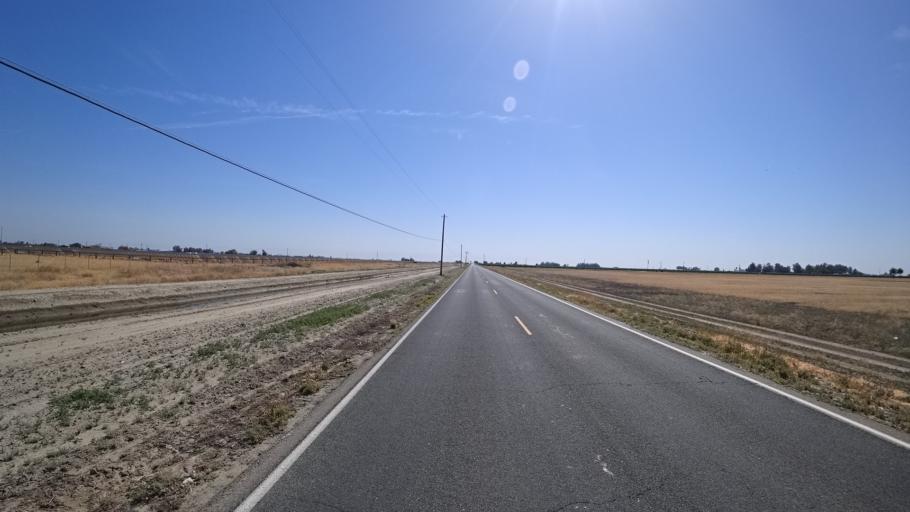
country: US
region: California
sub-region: Kings County
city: Stratford
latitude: 36.2115
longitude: -119.8019
